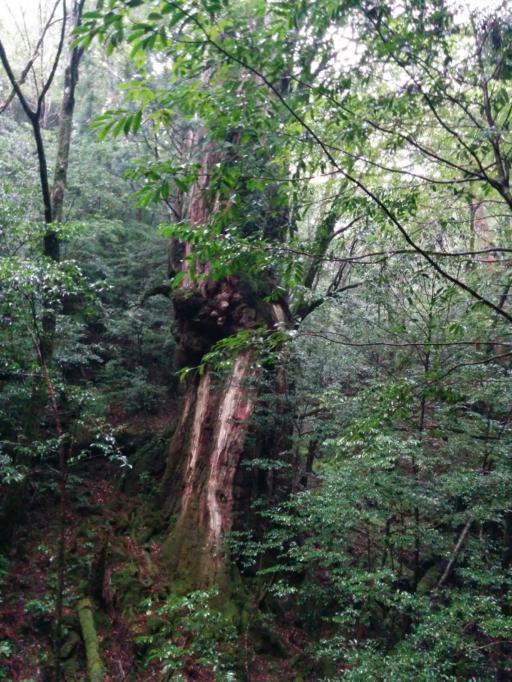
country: JP
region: Kagoshima
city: Nishinoomote
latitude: 30.3535
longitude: 130.5460
